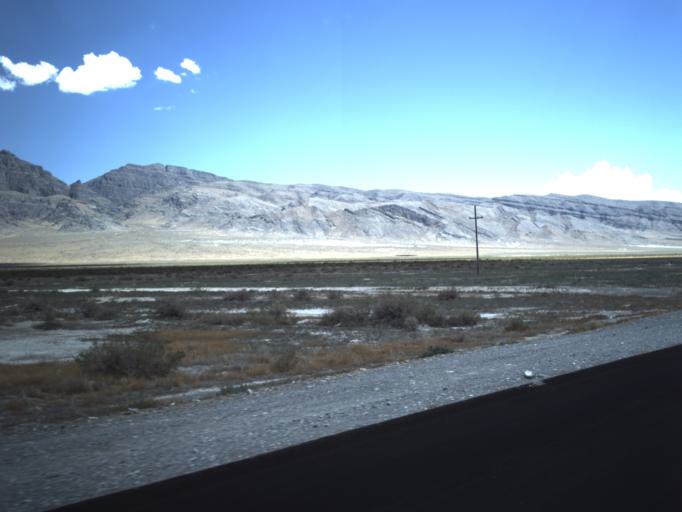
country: US
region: Utah
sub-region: Beaver County
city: Milford
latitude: 39.0765
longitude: -113.4775
